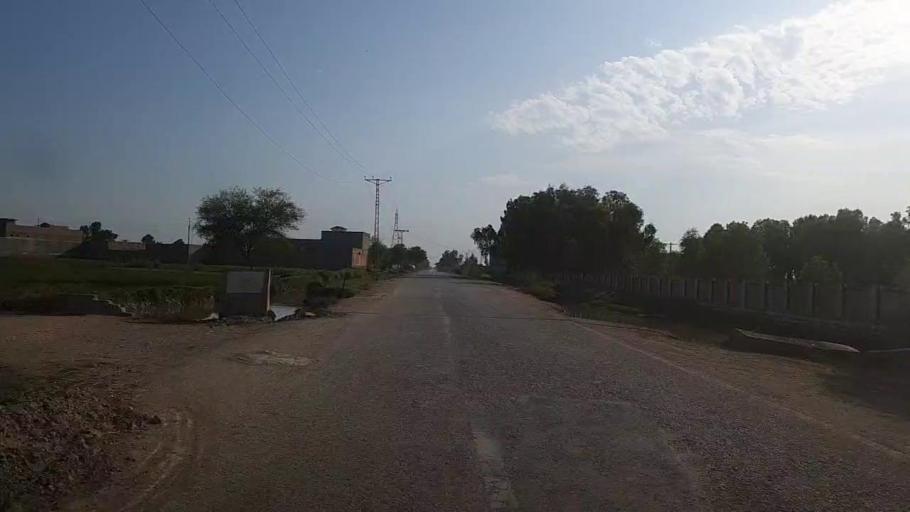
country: PK
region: Sindh
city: Thul
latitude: 28.2320
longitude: 68.7678
